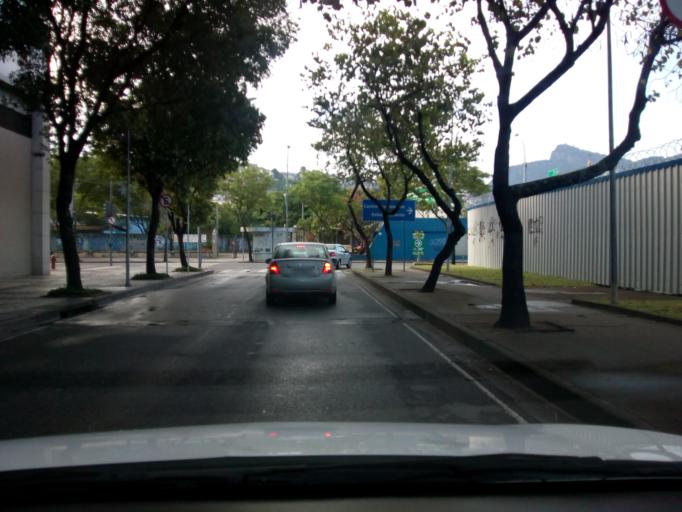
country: BR
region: Rio de Janeiro
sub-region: Rio De Janeiro
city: Rio de Janeiro
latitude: -22.9123
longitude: -43.2064
